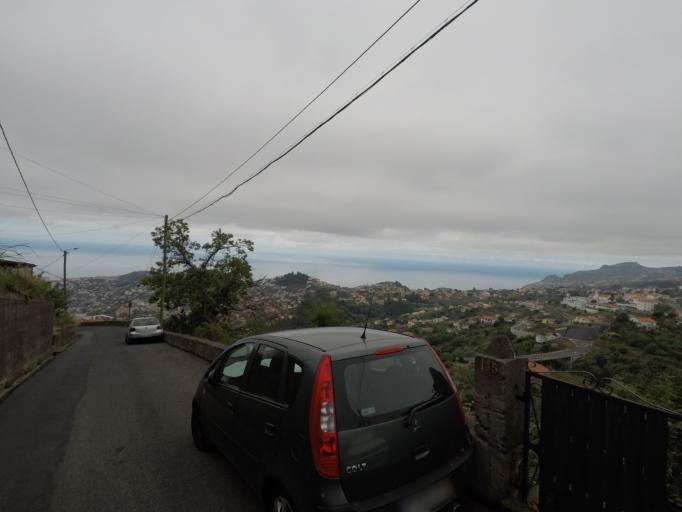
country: PT
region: Madeira
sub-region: Funchal
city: Nossa Senhora do Monte
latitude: 32.6799
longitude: -16.9391
